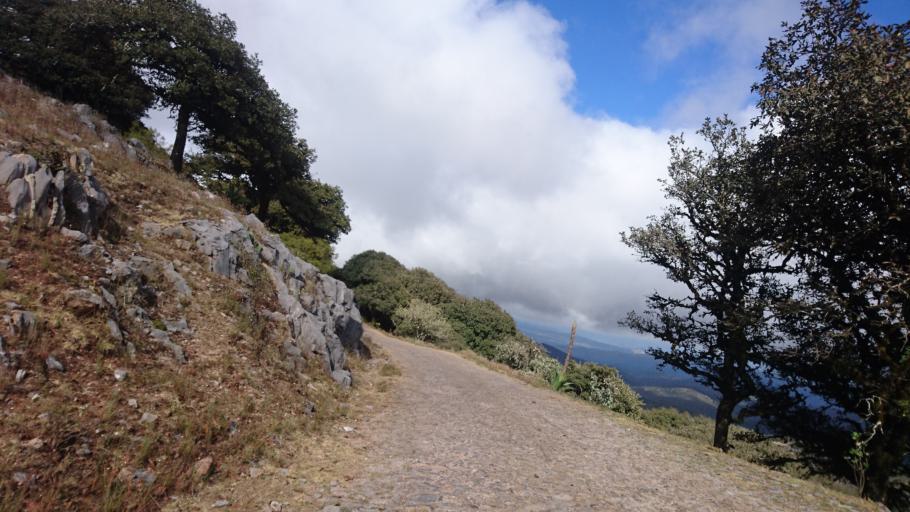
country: MX
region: San Luis Potosi
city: Zaragoza
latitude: 22.0661
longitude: -100.6395
